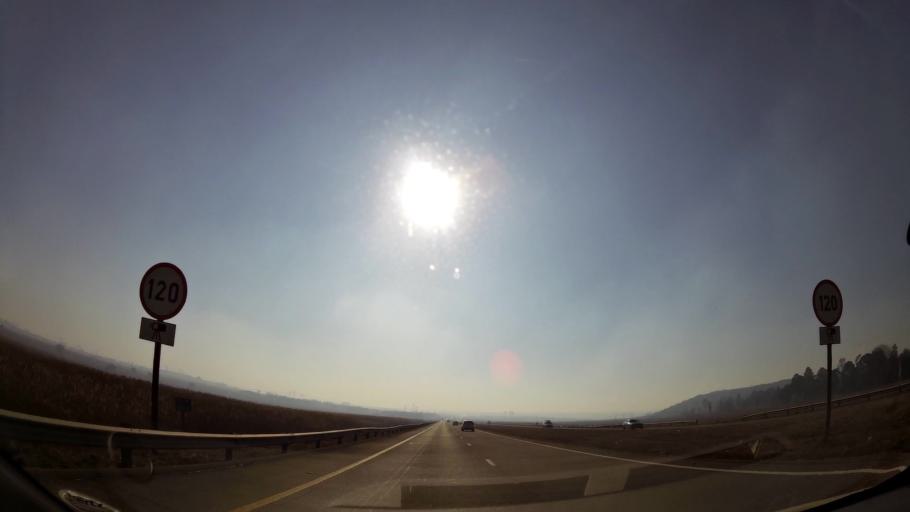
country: ZA
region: Mpumalanga
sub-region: Nkangala District Municipality
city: Witbank
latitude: -25.9416
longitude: 29.2029
